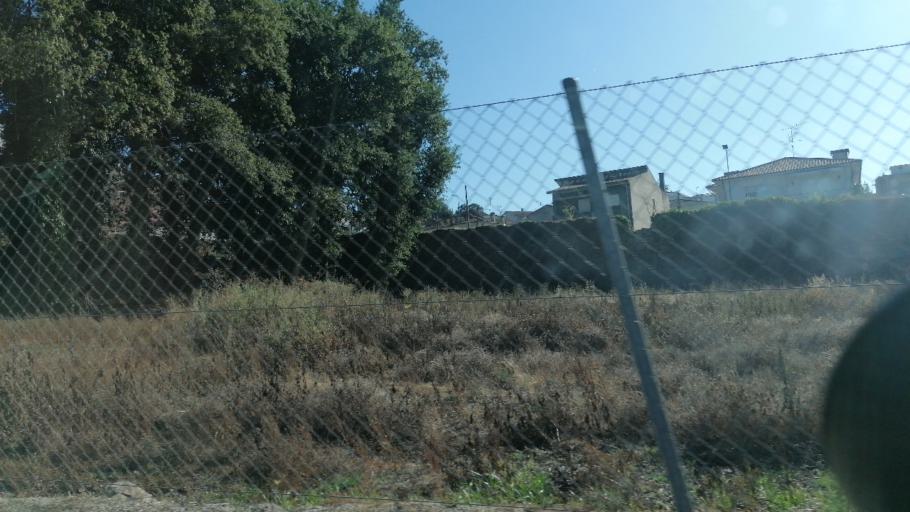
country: PT
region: Porto
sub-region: Santo Tirso
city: Santo Tirso
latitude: 41.3487
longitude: -8.4751
